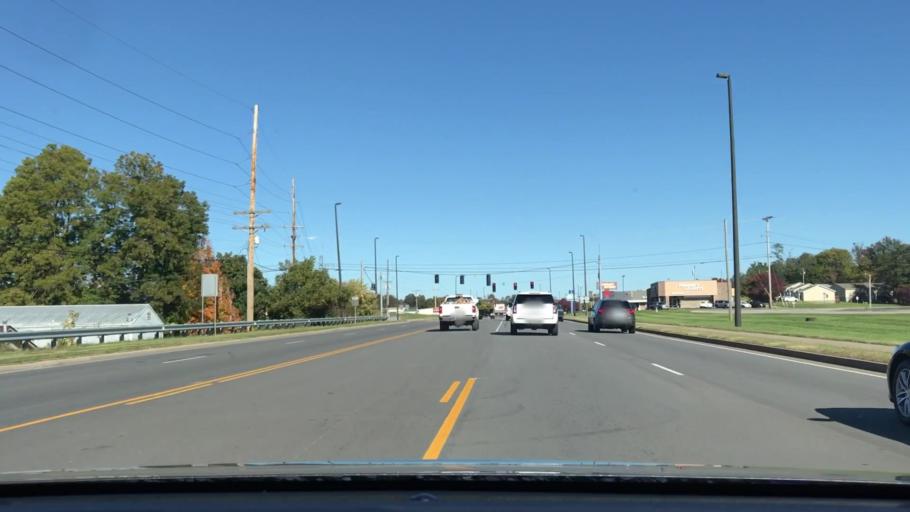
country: US
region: Kentucky
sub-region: Barren County
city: Glasgow
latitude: 36.9881
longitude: -85.9320
